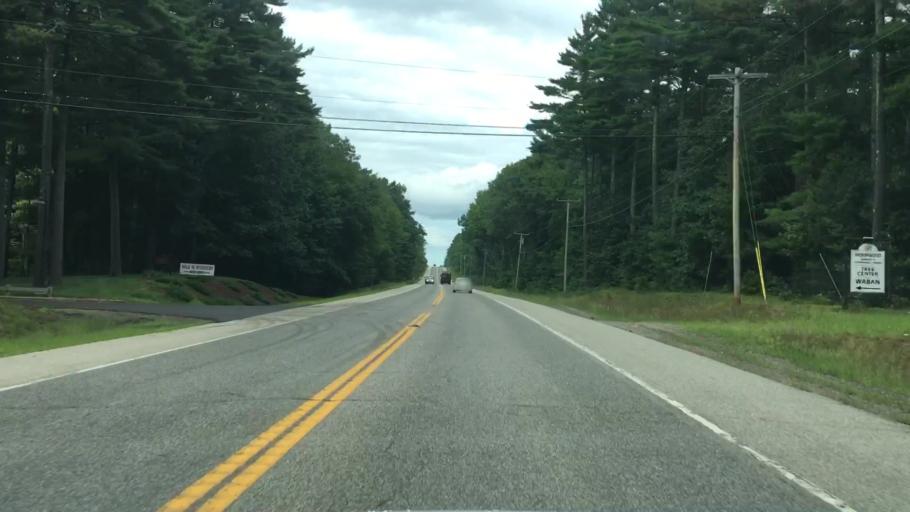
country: US
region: Maine
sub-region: York County
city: South Sanford
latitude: 43.3602
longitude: -70.7289
